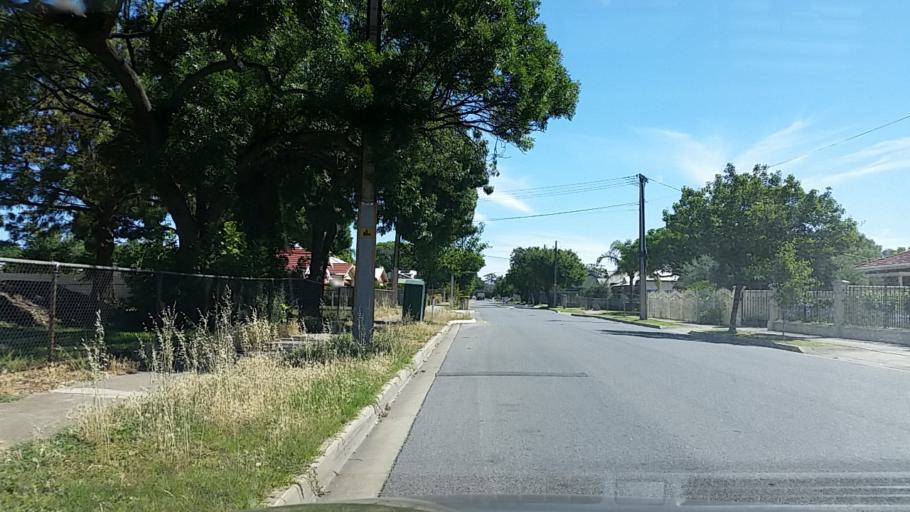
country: AU
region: South Australia
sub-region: Charles Sturt
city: Allenby Gardens
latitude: -34.8871
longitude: 138.5639
